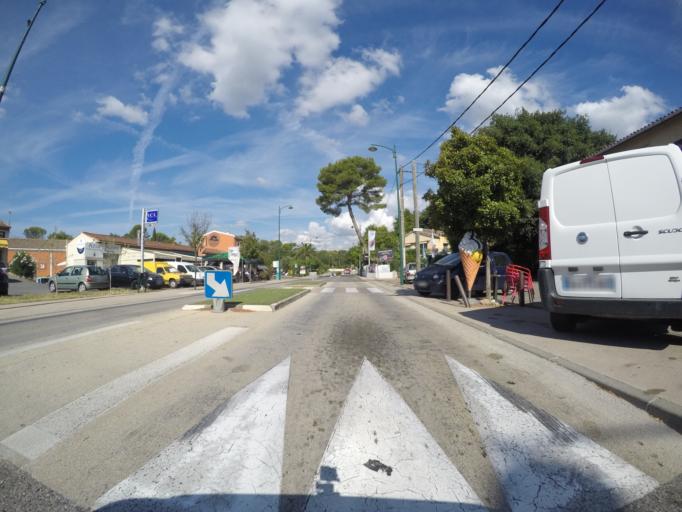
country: FR
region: Provence-Alpes-Cote d'Azur
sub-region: Departement des Alpes-Maritimes
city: Le Rouret
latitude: 43.6677
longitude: 7.0452
